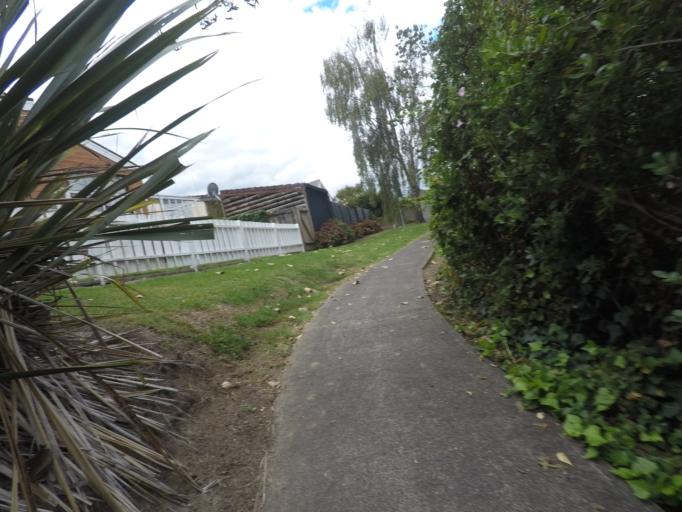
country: NZ
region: Auckland
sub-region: Auckland
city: Papakura
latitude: -37.0597
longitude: 174.9339
